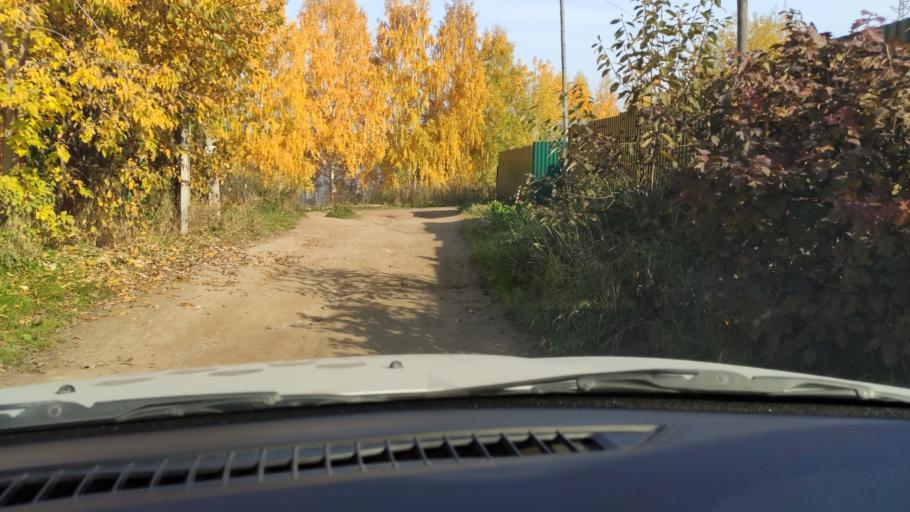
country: RU
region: Perm
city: Sylva
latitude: 58.0482
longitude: 56.7345
